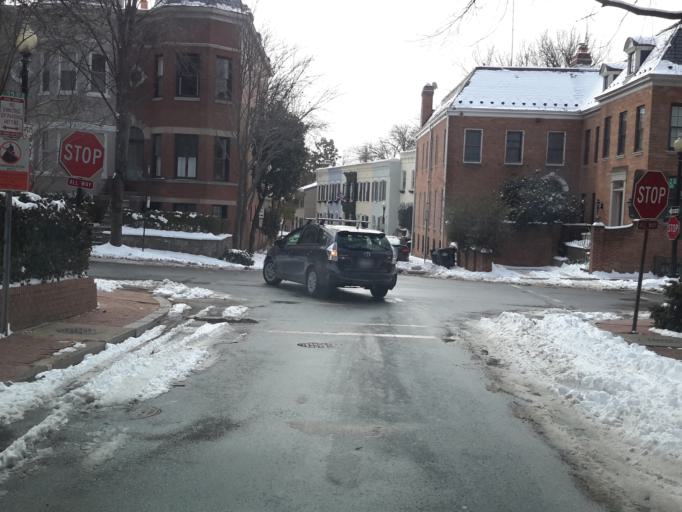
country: US
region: Washington, D.C.
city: Washington, D.C.
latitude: 38.9106
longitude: -77.0638
